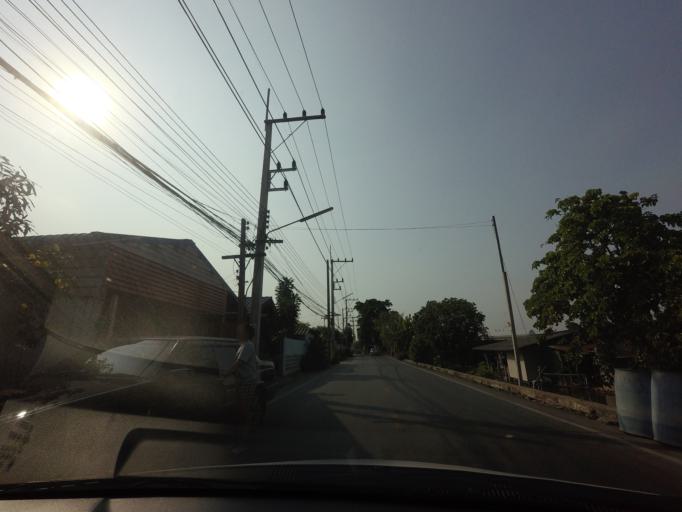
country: TH
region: Samut Sakhon
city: Krathum Baen
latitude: 13.6943
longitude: 100.2512
